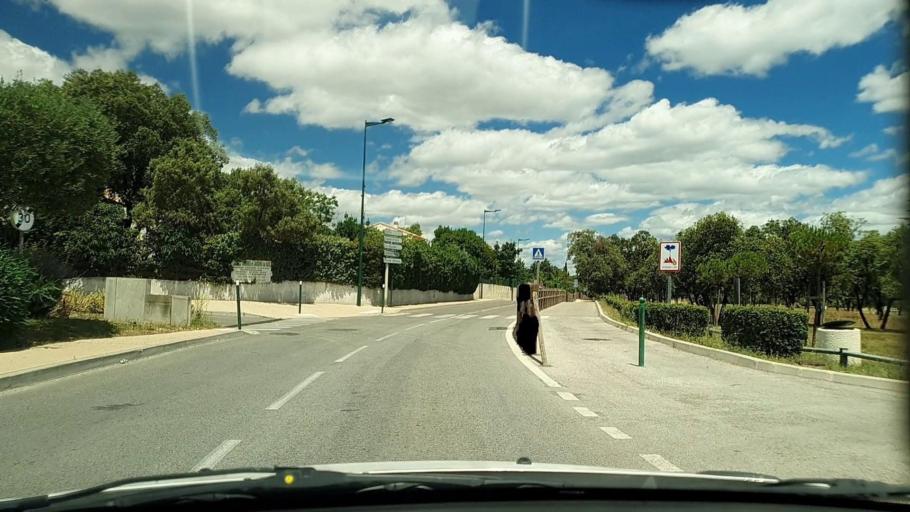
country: FR
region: Languedoc-Roussillon
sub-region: Departement du Gard
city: Poulx
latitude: 43.9011
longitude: 4.4207
